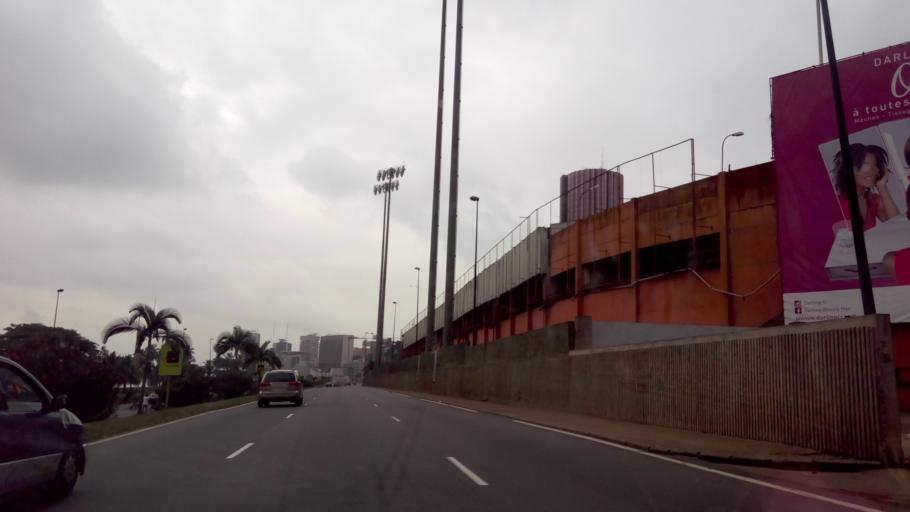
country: CI
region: Lagunes
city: Abidjan
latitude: 5.3295
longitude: -4.0183
